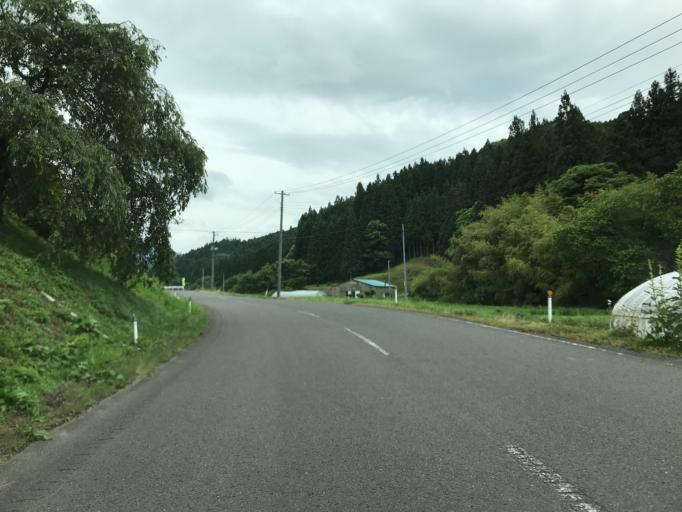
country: JP
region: Fukushima
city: Funehikimachi-funehiki
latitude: 37.4083
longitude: 140.6554
